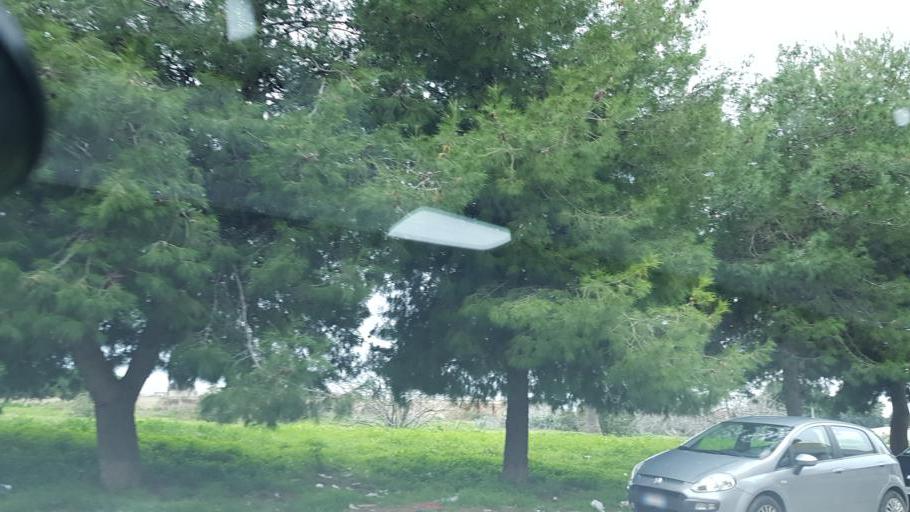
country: IT
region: Apulia
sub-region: Provincia di Brindisi
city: Brindisi
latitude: 40.6296
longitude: 17.9544
